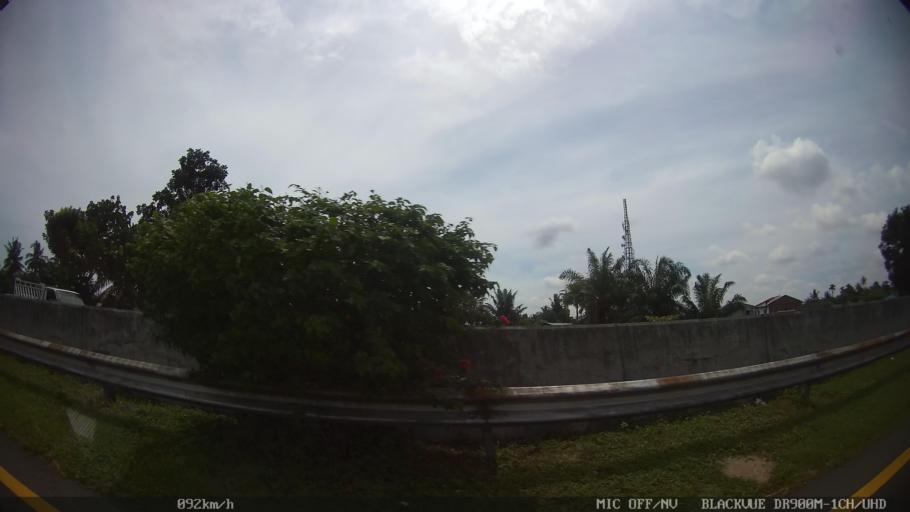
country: ID
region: North Sumatra
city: Labuhan Deli
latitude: 3.7083
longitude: 98.6818
